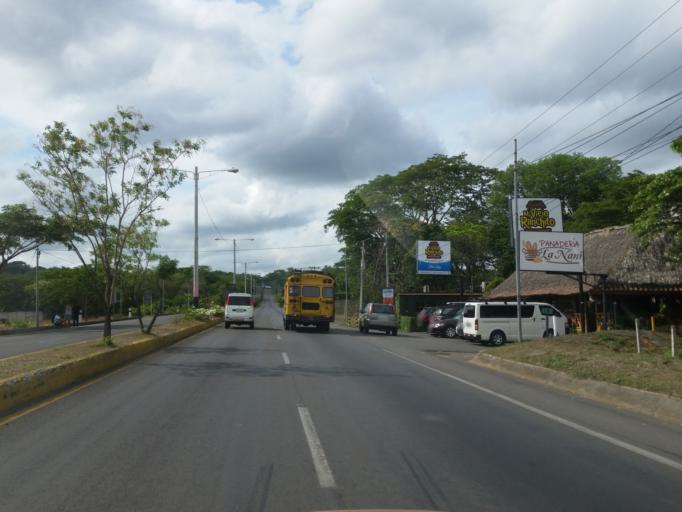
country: NI
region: Masaya
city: Ticuantepe
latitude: 12.0348
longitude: -86.1840
